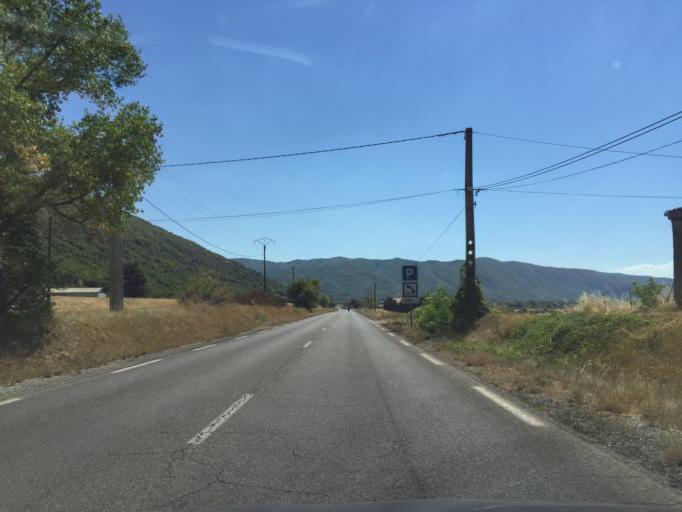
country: FR
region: Provence-Alpes-Cote d'Azur
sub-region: Departement des Alpes-de-Haute-Provence
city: Malijai
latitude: 44.0676
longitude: 6.0219
